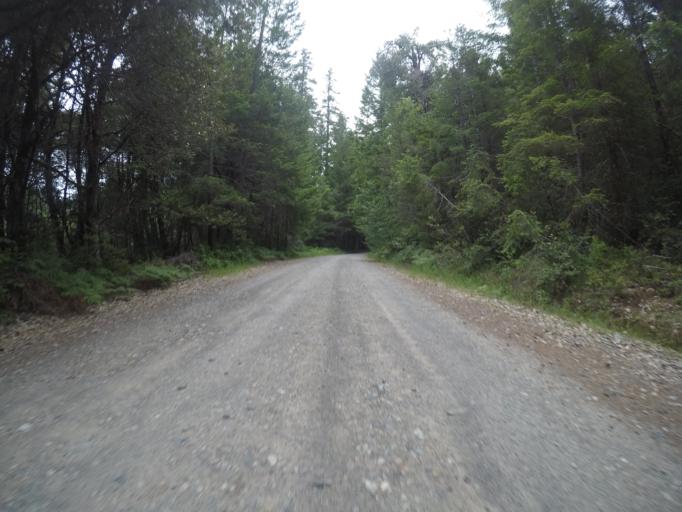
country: US
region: California
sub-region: Del Norte County
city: Bertsch-Oceanview
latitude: 41.6957
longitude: -123.9017
